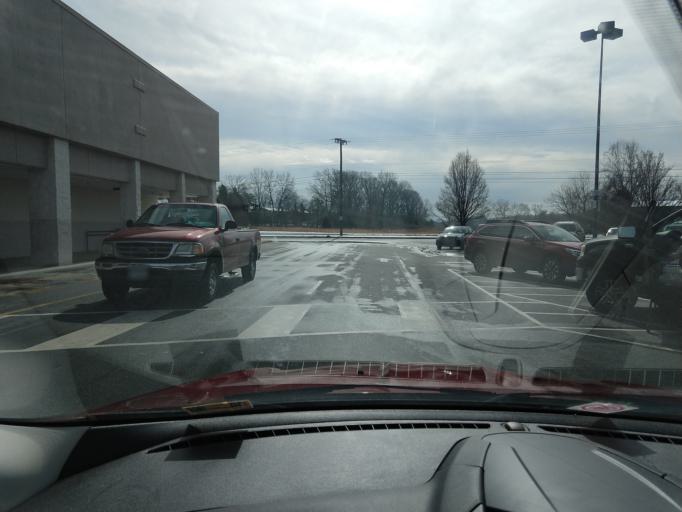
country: US
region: Virginia
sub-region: Amherst County
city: Madison Heights
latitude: 37.4672
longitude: -79.1165
